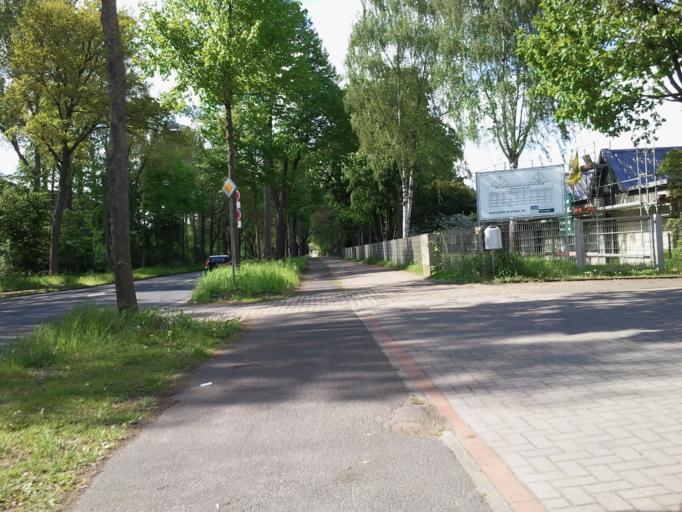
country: DE
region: Lower Saxony
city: Ritterhude
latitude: 53.1385
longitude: 8.7227
